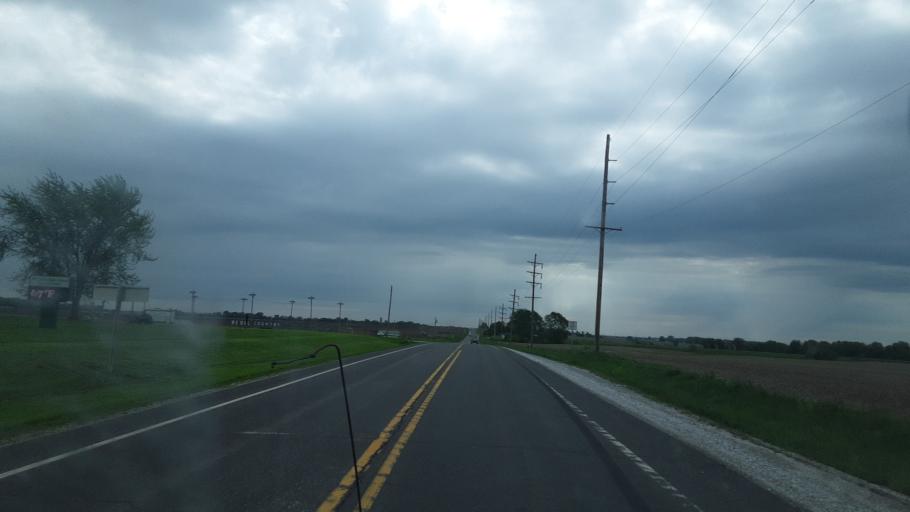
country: US
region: Illinois
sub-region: Fulton County
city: Astoria
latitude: 40.3568
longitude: -90.4197
